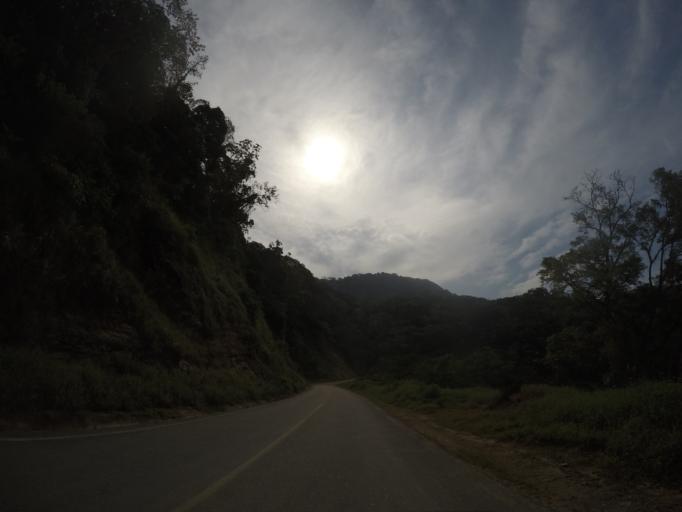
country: MX
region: Oaxaca
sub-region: San Pedro Pochutla
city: Los Naranjos Esquipulas
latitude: 15.9566
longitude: -96.4514
